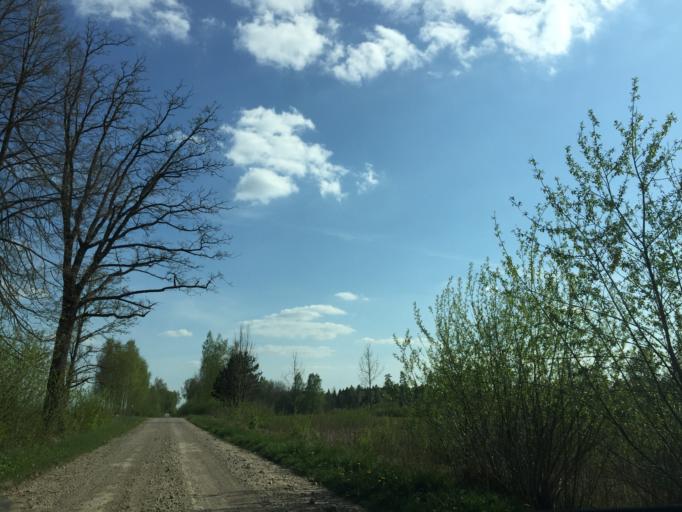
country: LV
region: Lecava
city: Iecava
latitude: 56.5077
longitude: 24.3179
